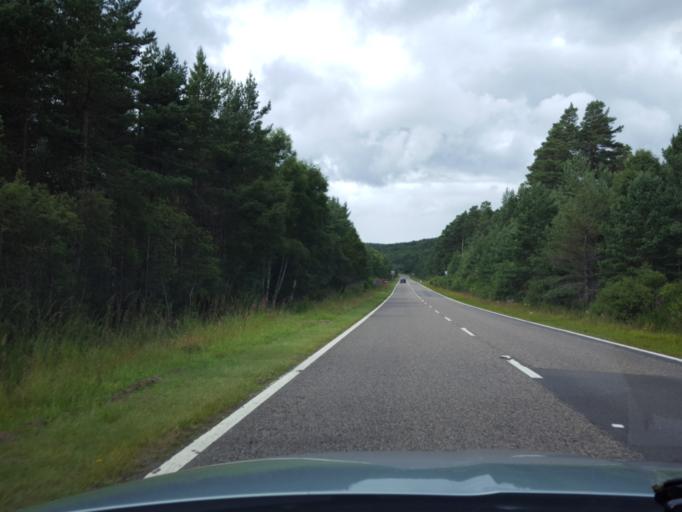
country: GB
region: Scotland
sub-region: Highland
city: Grantown on Spey
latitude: 57.2819
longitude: -3.6918
